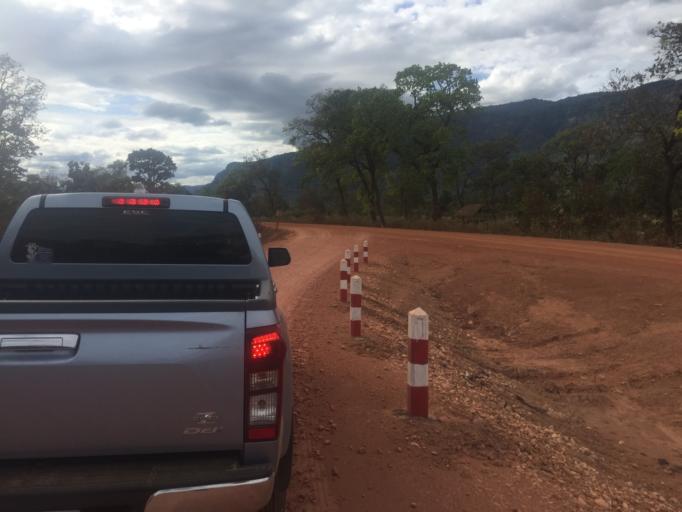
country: LA
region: Attapu
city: Attapu
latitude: 14.7672
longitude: 106.7296
